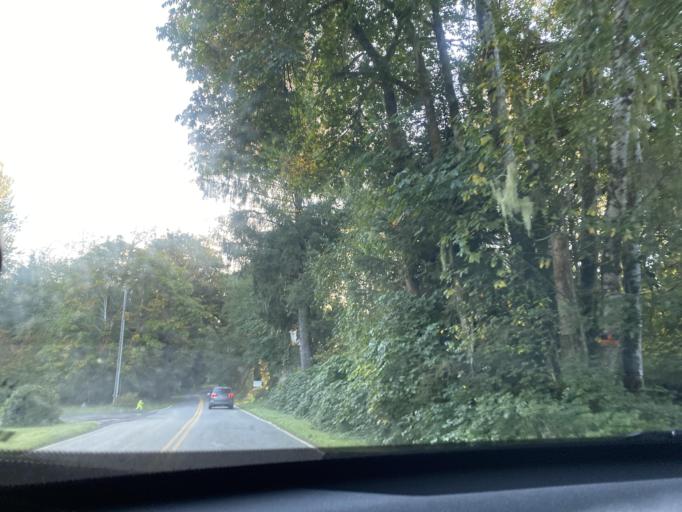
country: US
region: Washington
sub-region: Clallam County
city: Forks
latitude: 47.8168
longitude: -124.1542
